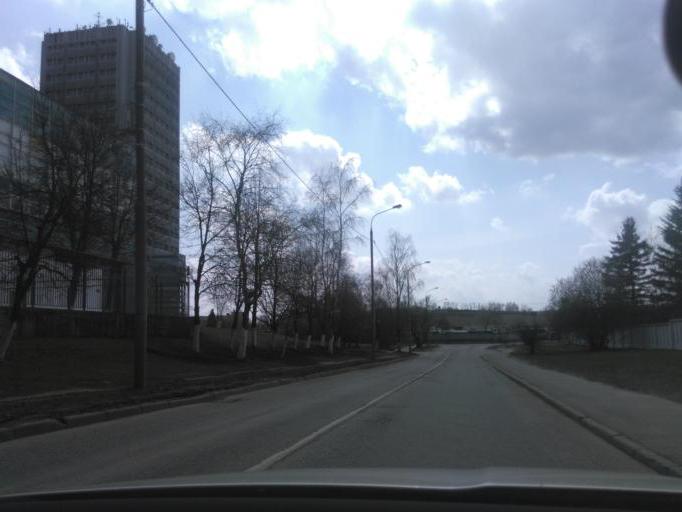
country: RU
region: Moskovskaya
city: Mendeleyevo
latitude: 56.0147
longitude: 37.1917
